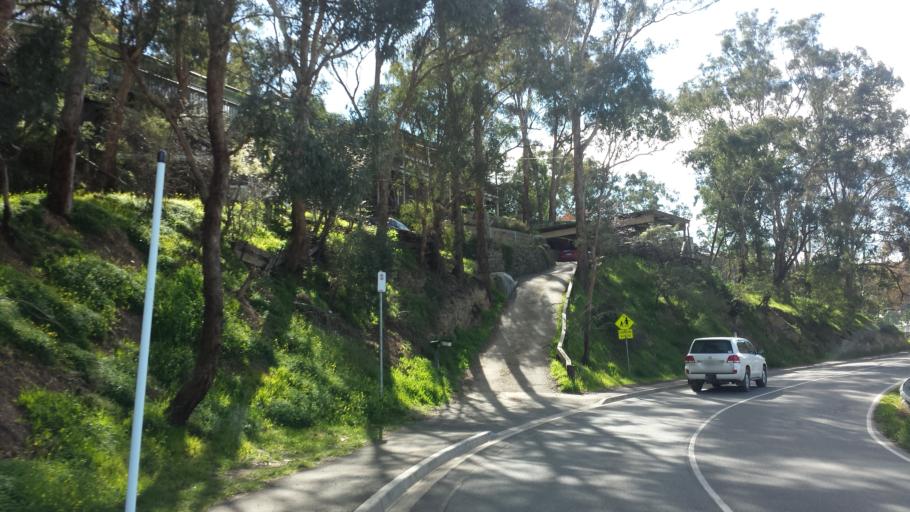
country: AU
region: Victoria
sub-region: Nillumbik
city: Hurstbridge
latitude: -37.6348
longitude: 145.1915
